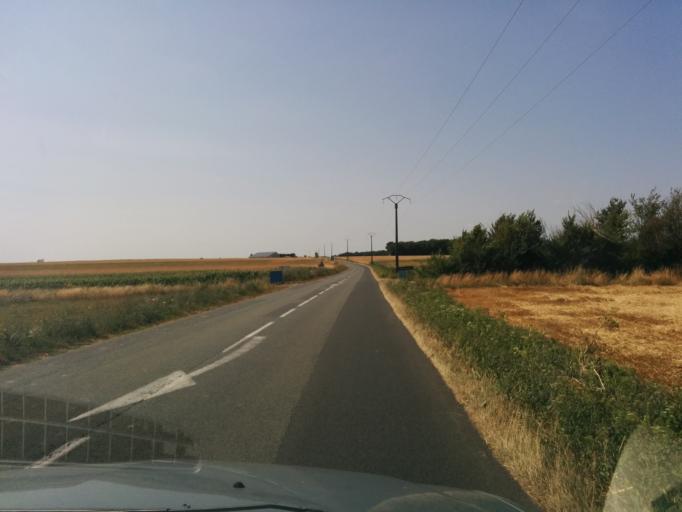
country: FR
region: Poitou-Charentes
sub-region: Departement de la Vienne
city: Mirebeau
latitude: 46.7336
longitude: 0.1915
